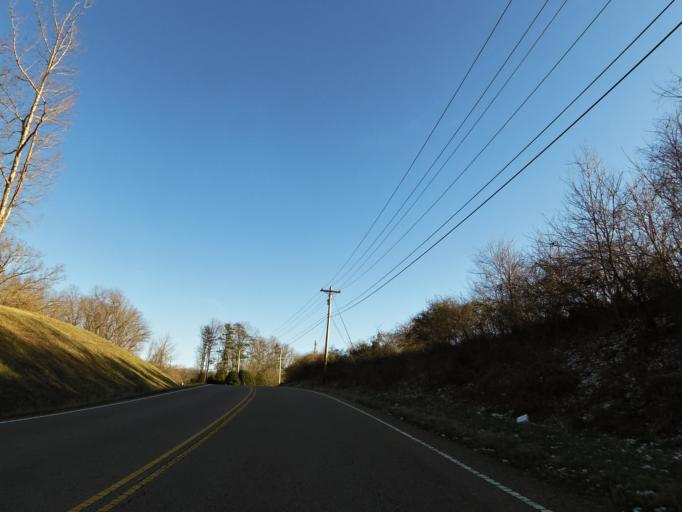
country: US
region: Tennessee
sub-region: Knox County
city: Farragut
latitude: 35.8813
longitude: -84.0949
